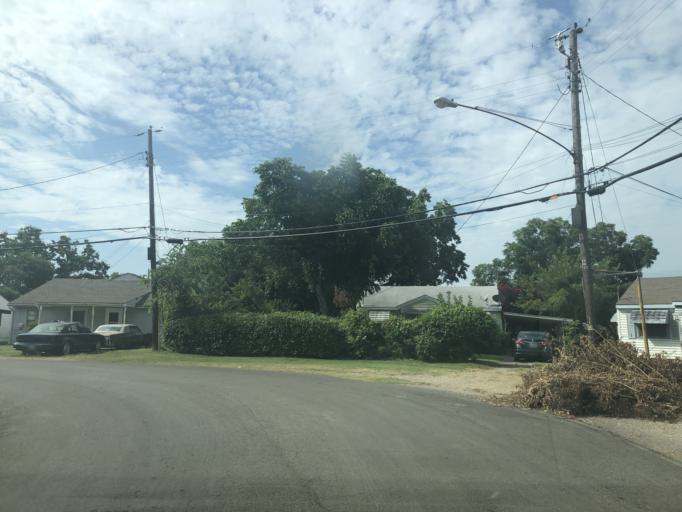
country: US
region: Texas
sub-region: Dallas County
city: Dallas
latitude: 32.8151
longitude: -96.8502
